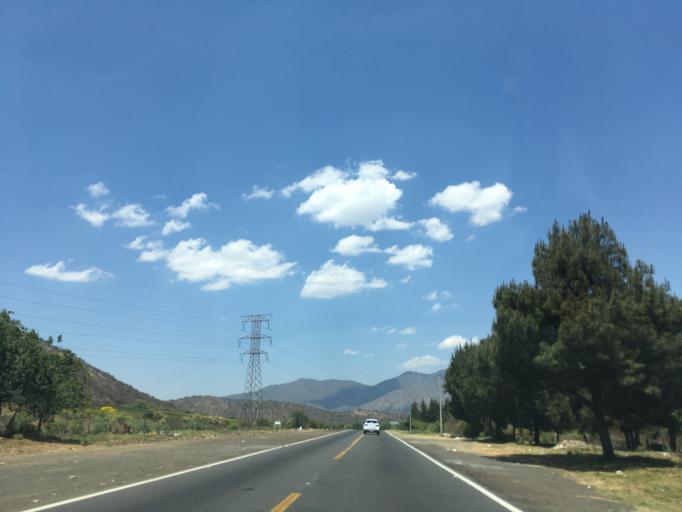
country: MX
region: Michoacan
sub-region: Chilchota
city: Tacuro (Santa Maria Tacuro)
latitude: 19.8248
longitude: -102.0279
